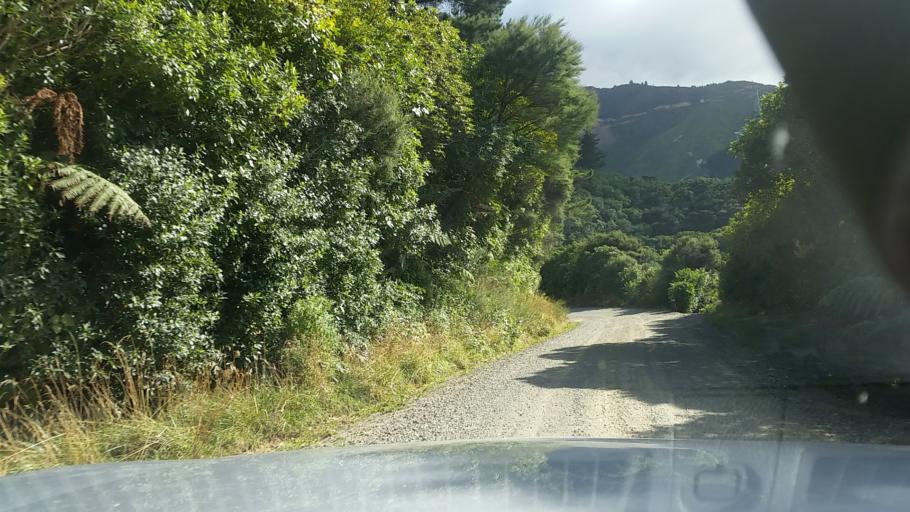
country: NZ
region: Marlborough
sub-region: Marlborough District
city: Picton
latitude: -41.2885
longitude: 174.1305
